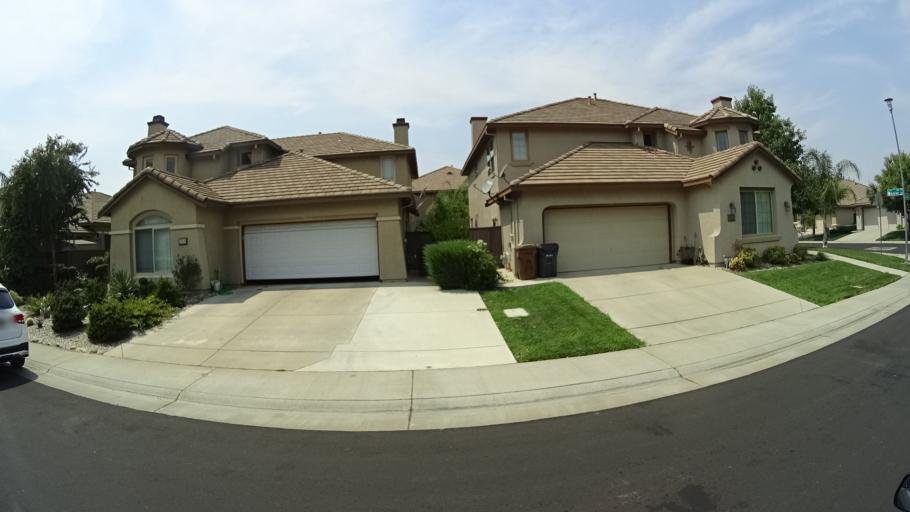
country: US
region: California
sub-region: Sacramento County
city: Laguna
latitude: 38.3823
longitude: -121.4273
